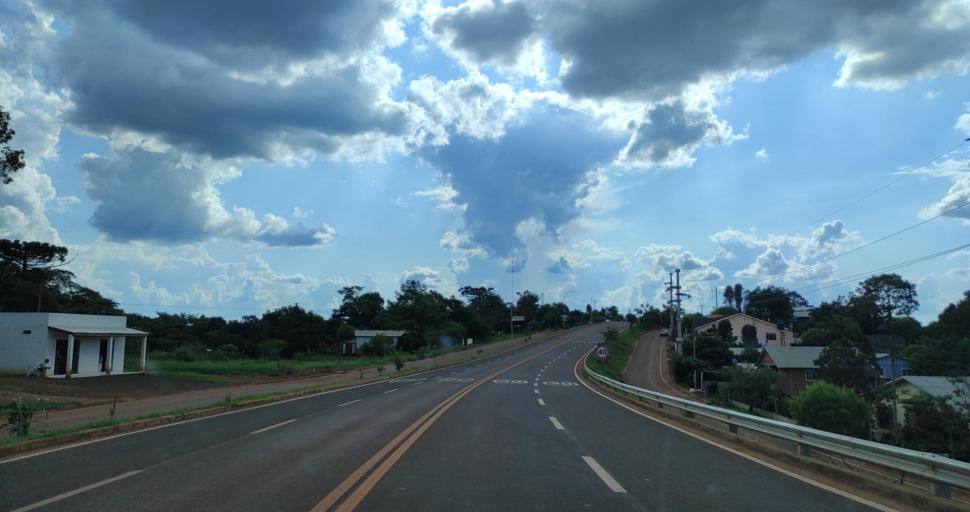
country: AR
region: Misiones
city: Bernardo de Irigoyen
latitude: -26.2954
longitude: -53.7489
